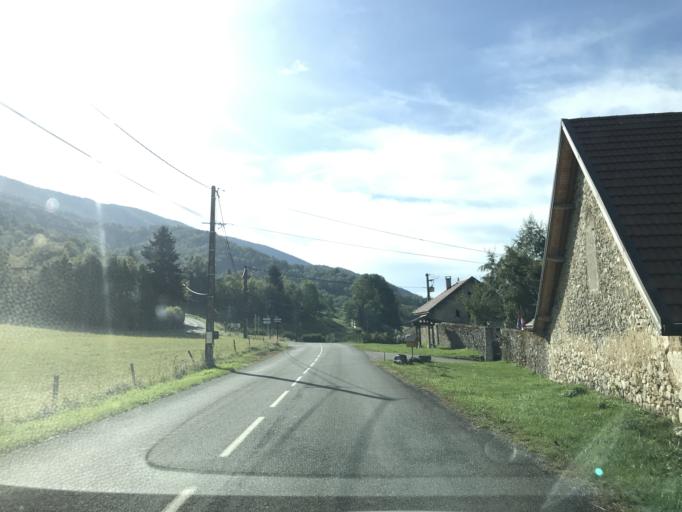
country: FR
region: Rhone-Alpes
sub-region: Departement de la Savoie
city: Novalaise
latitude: 45.6523
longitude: 5.7892
